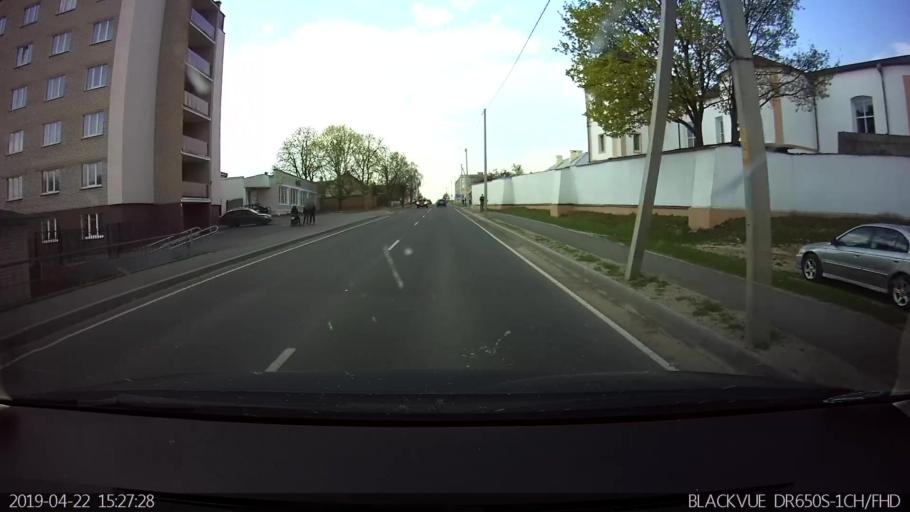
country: BY
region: Brest
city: Vysokaye
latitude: 52.3709
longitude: 23.3711
